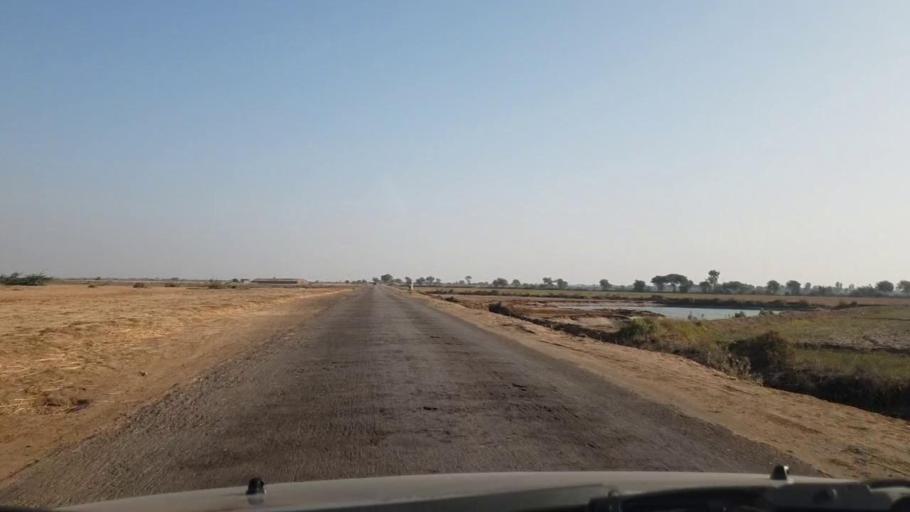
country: PK
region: Sindh
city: Tando Bago
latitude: 24.8169
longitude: 69.0019
